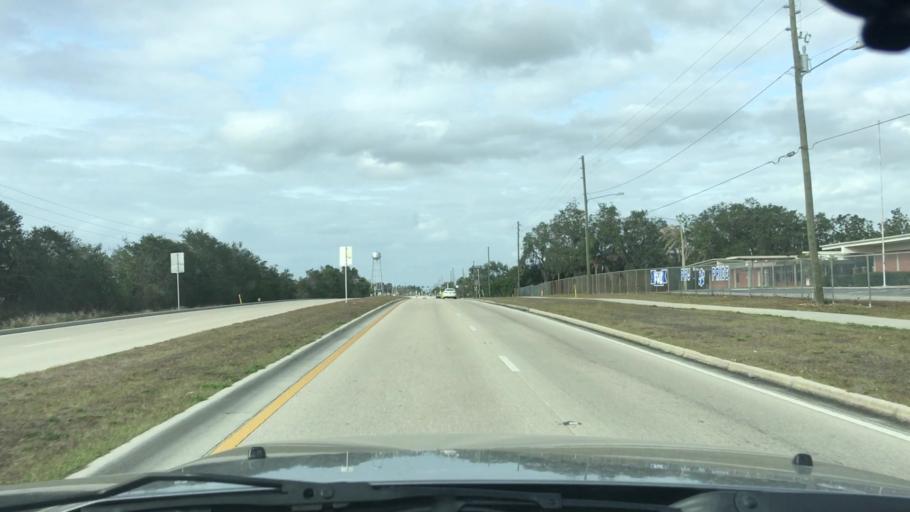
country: US
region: Florida
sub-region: Highlands County
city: Sebring
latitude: 27.4807
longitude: -81.4335
